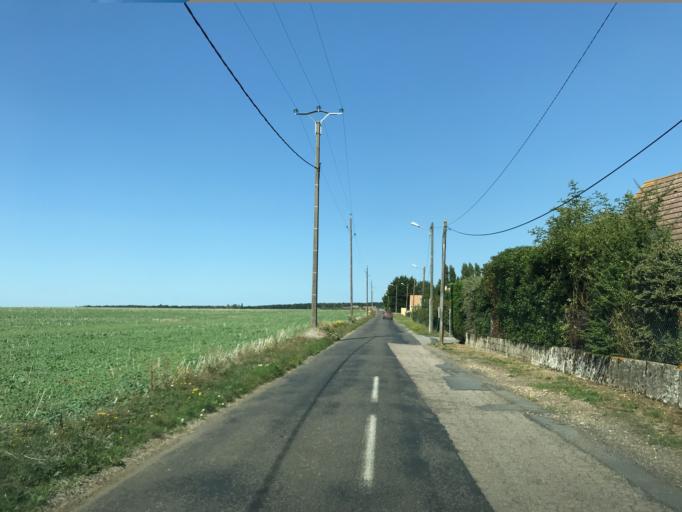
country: FR
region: Haute-Normandie
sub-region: Departement de l'Eure
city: Houlbec-Cocherel
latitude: 49.0603
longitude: 1.2705
